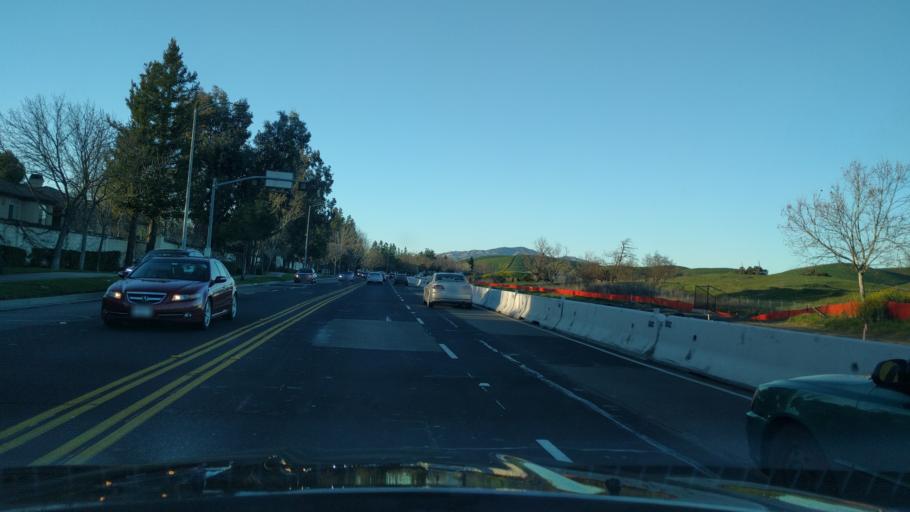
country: US
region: California
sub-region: Alameda County
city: Dublin
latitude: 37.7264
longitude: -121.9100
